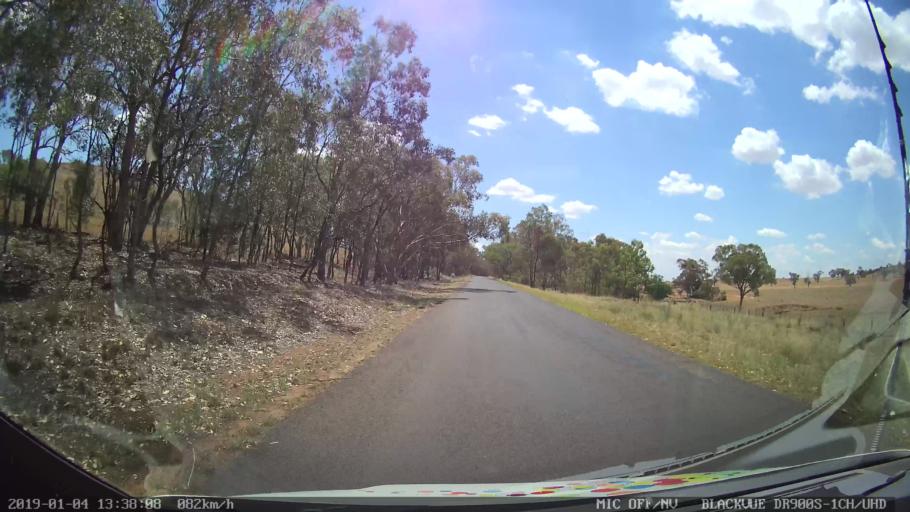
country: AU
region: New South Wales
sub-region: Dubbo Municipality
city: Dubbo
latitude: -32.5416
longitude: 148.5465
